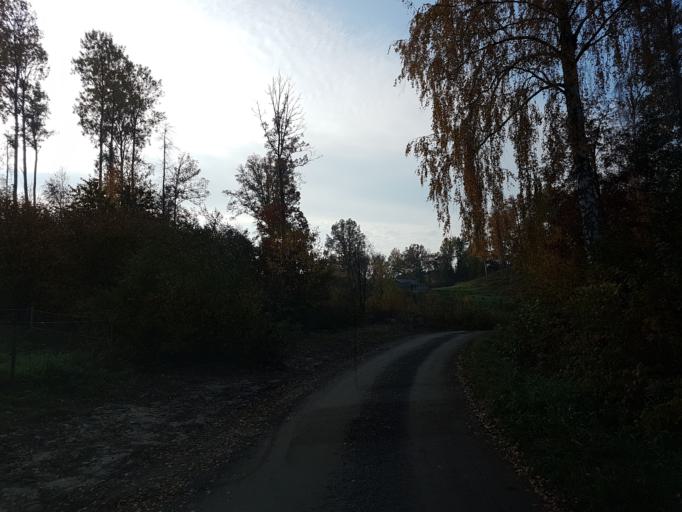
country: SE
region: OEstergoetland
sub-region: Atvidabergs Kommun
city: Atvidaberg
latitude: 58.1835
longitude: 16.0612
